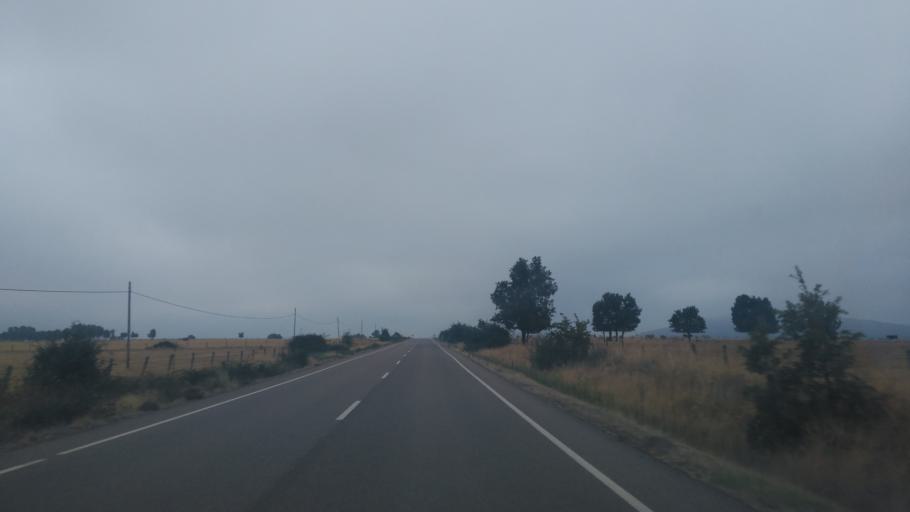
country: ES
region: Castille and Leon
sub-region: Provincia de Salamanca
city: Tamames
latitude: 40.6398
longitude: -6.1119
